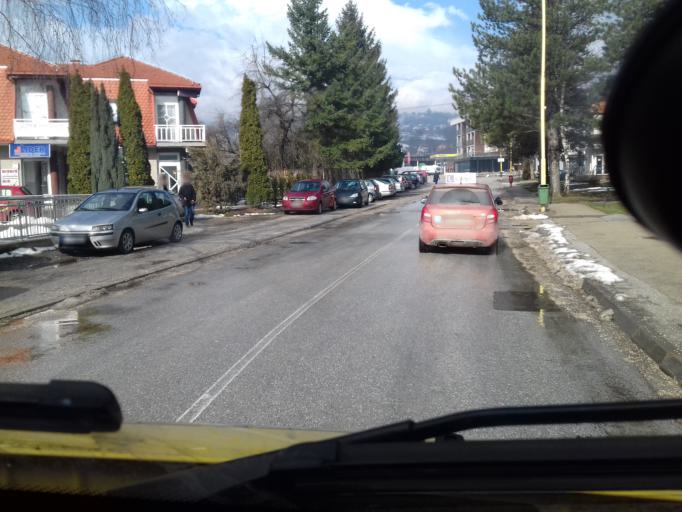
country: BA
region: Federation of Bosnia and Herzegovina
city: Zepce
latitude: 44.4244
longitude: 18.0306
